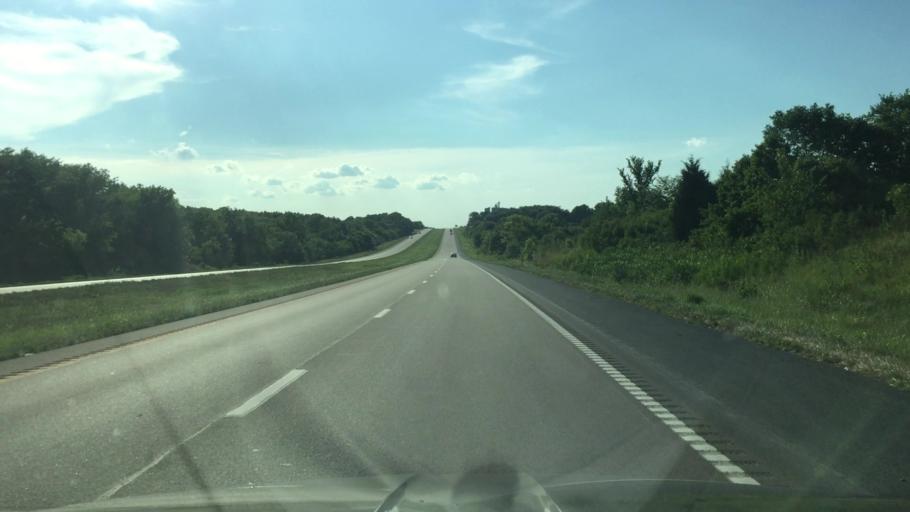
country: US
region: Missouri
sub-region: Pettis County
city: Sedalia
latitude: 38.7411
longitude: -93.3233
